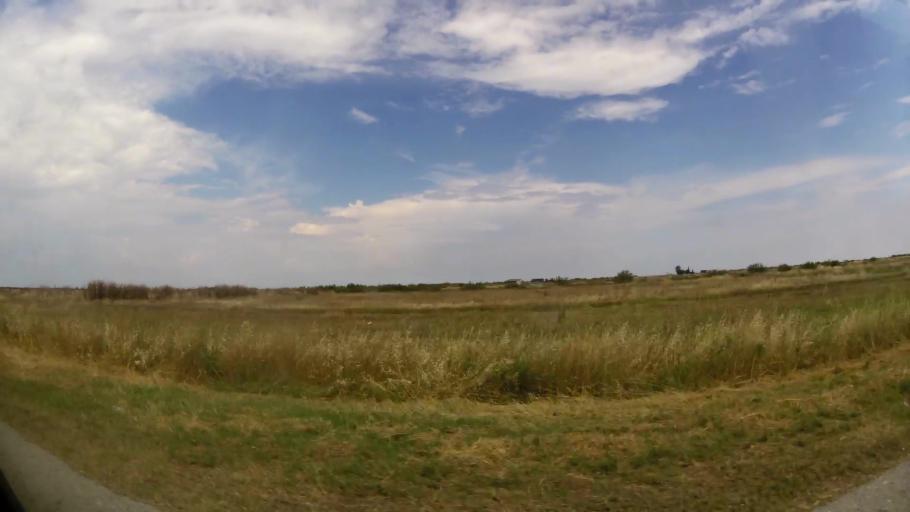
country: GR
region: Central Macedonia
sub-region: Nomos Pierias
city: Korinos
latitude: 40.3212
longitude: 22.6220
